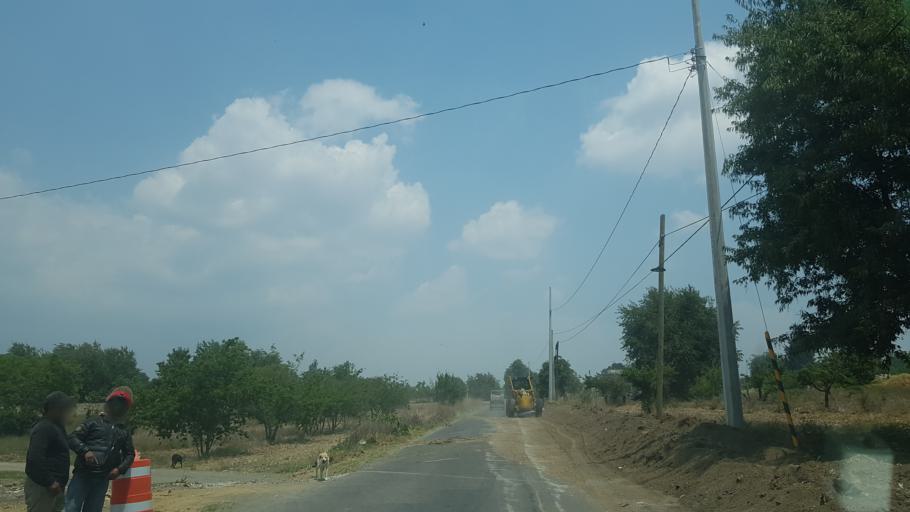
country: MX
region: Puebla
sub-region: San Nicolas de los Ranchos
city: San Pedro Yancuitlalpan
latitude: 19.0855
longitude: -98.4814
